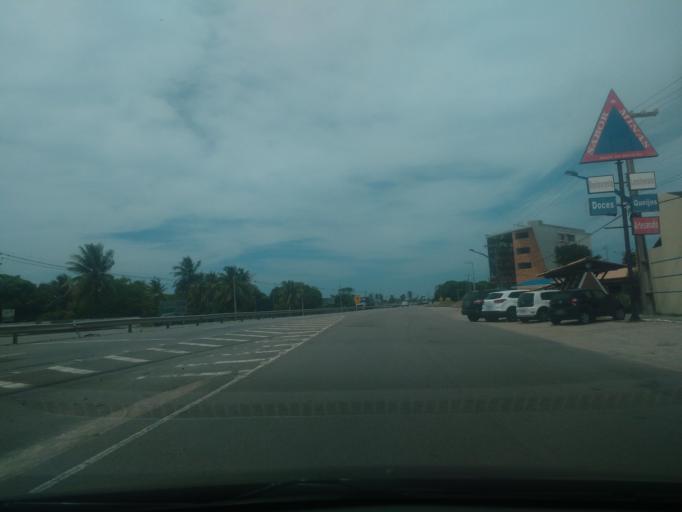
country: BR
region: Alagoas
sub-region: Marechal Deodoro
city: Marechal Deodoro
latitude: -9.7653
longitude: -35.8489
